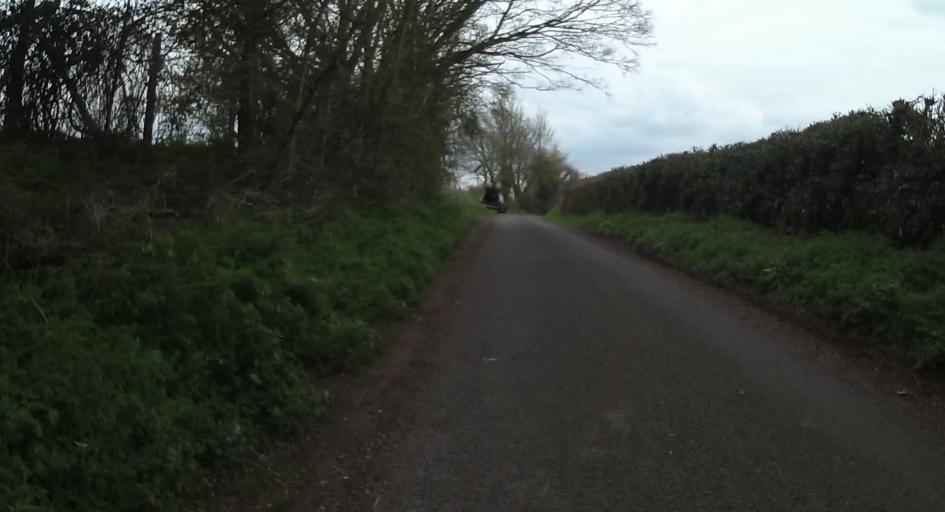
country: GB
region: England
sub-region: Hampshire
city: Long Sutton
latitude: 51.2246
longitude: -0.9670
